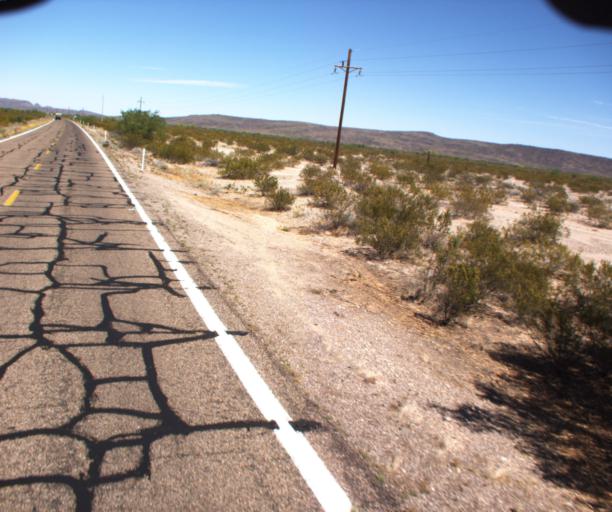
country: US
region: Arizona
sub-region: Pima County
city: Ajo
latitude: 32.4530
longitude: -112.8716
